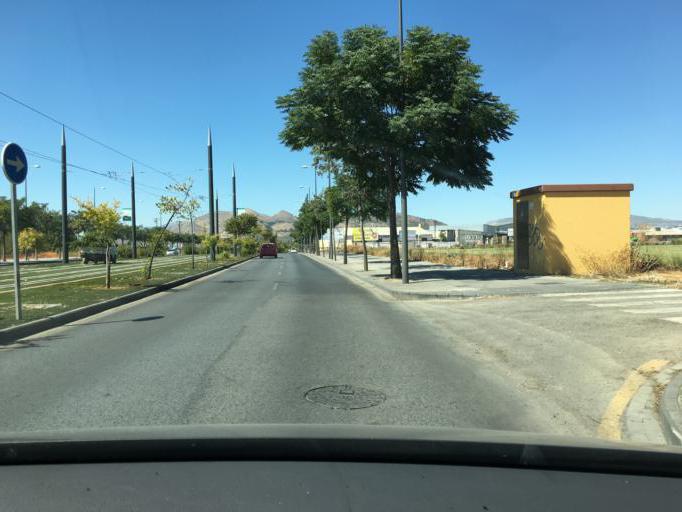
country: ES
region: Andalusia
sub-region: Provincia de Granada
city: Maracena
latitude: 37.2153
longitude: -3.6378
